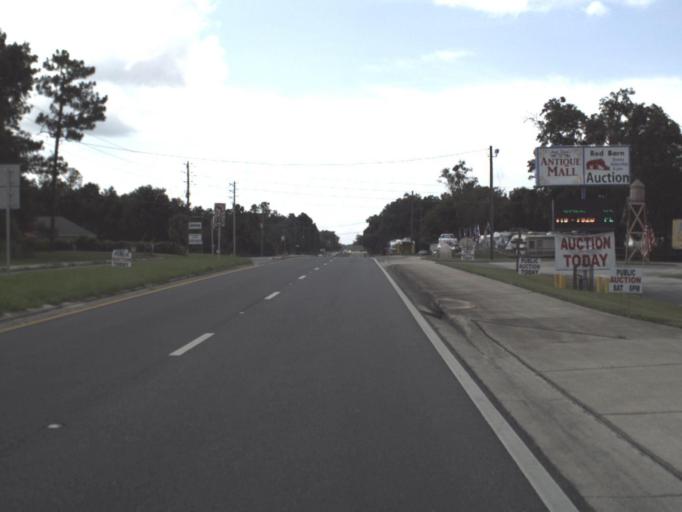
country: US
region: Florida
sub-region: Citrus County
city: Inverness Highlands South
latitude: 28.7956
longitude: -82.3056
